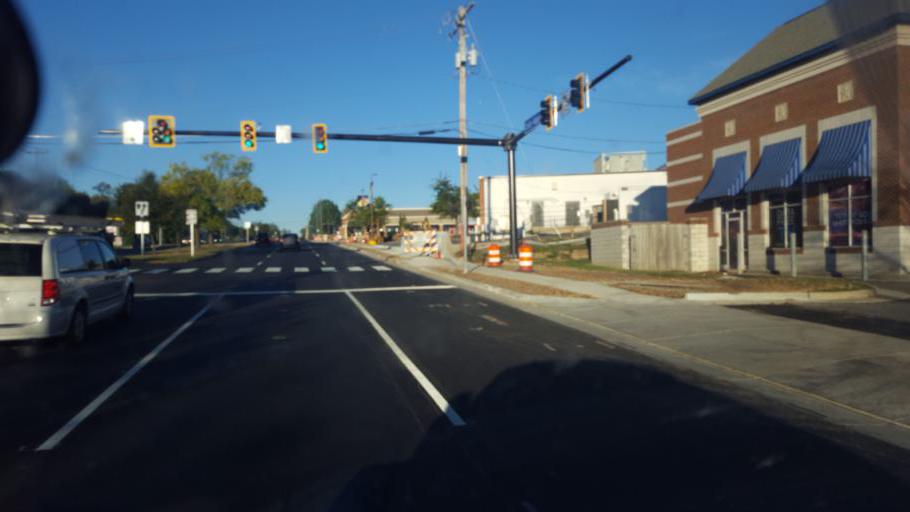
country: US
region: Virginia
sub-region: City of Fairfax
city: Fairfax
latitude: 38.8527
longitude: -77.3251
